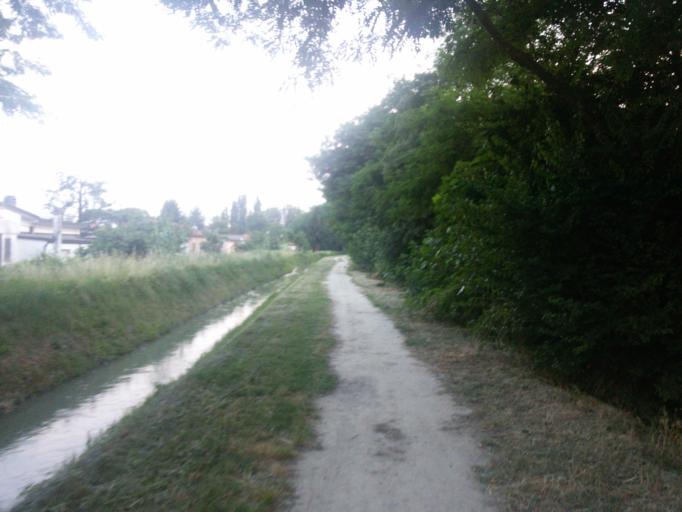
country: IT
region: Emilia-Romagna
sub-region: Provincia di Ravenna
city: Lugo
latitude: 44.4215
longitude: 11.9013
